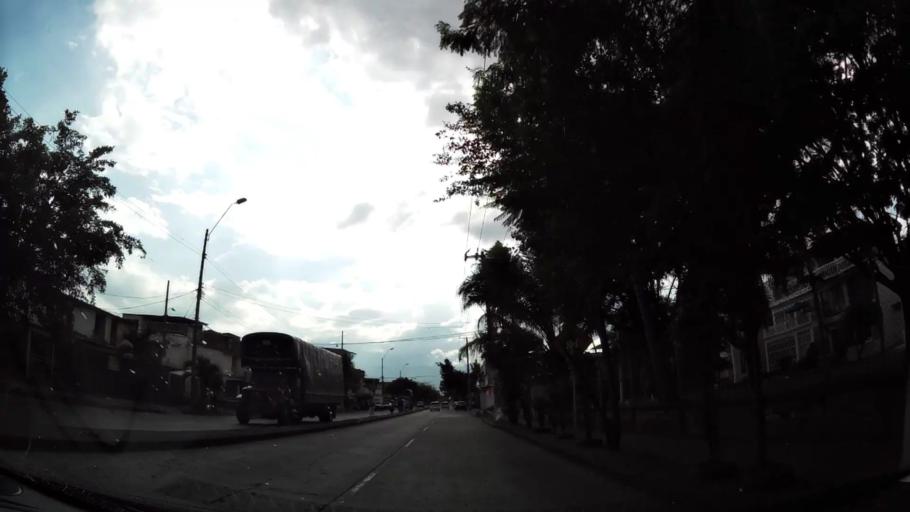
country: CO
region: Valle del Cauca
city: Cali
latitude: 3.4668
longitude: -76.4874
